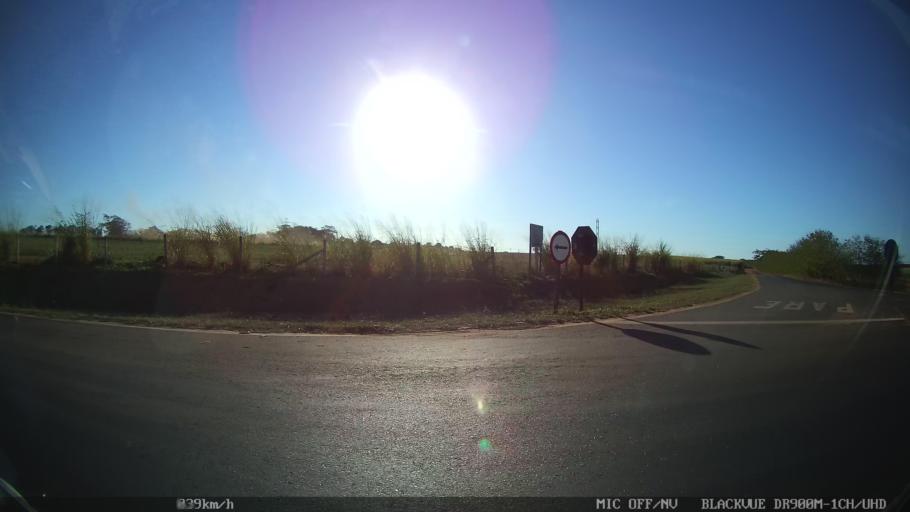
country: BR
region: Sao Paulo
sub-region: Guapiacu
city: Guapiacu
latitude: -20.7718
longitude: -49.2252
